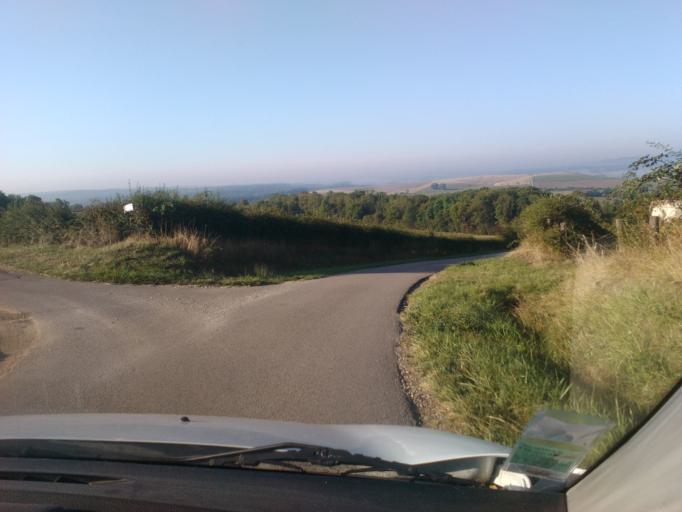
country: FR
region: Lorraine
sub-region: Departement des Vosges
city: Mirecourt
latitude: 48.2674
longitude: 6.1834
